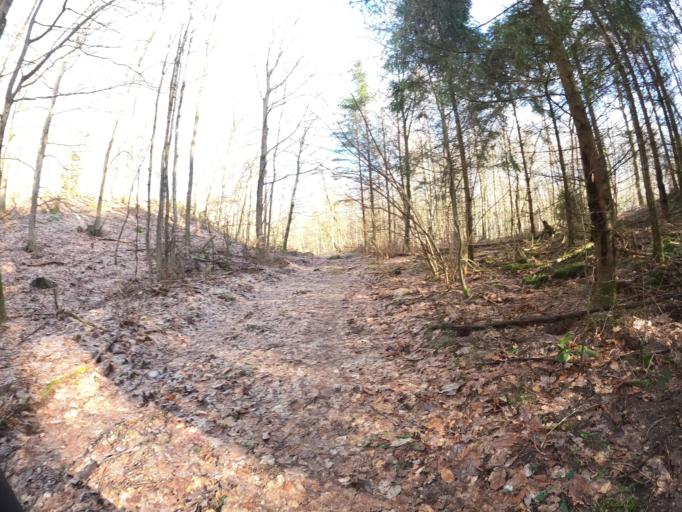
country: PL
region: West Pomeranian Voivodeship
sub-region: Powiat koszalinski
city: Polanow
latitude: 54.1286
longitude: 16.7724
